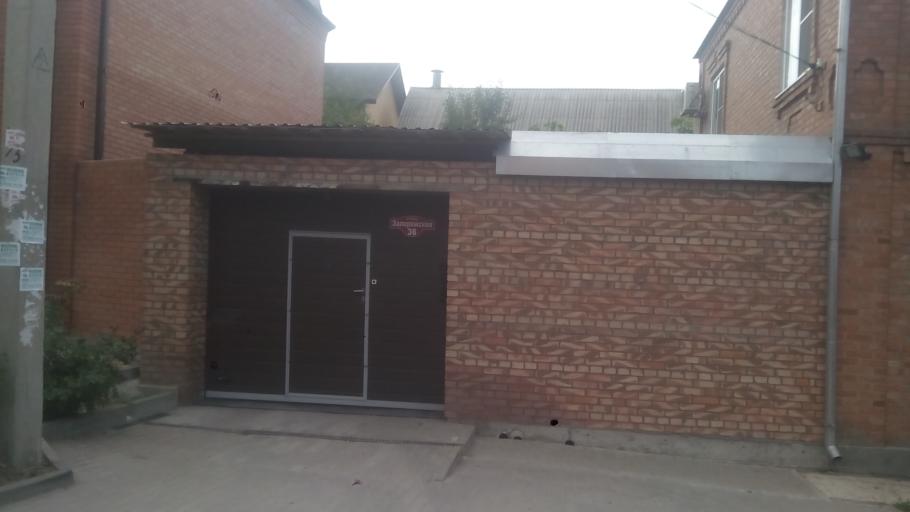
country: RU
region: Rostov
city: Rostov-na-Donu
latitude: 47.2189
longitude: 39.6484
